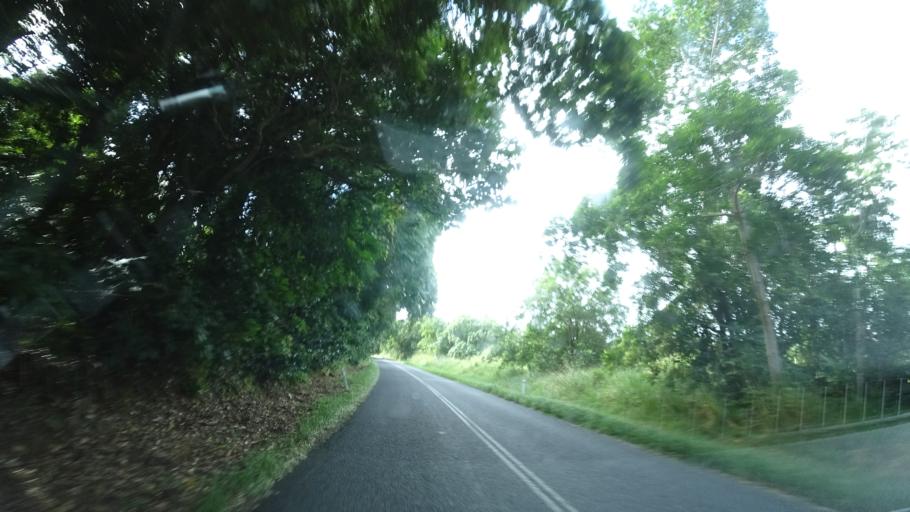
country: AU
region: Queensland
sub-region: Cairns
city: Port Douglas
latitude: -16.1043
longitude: 145.4576
